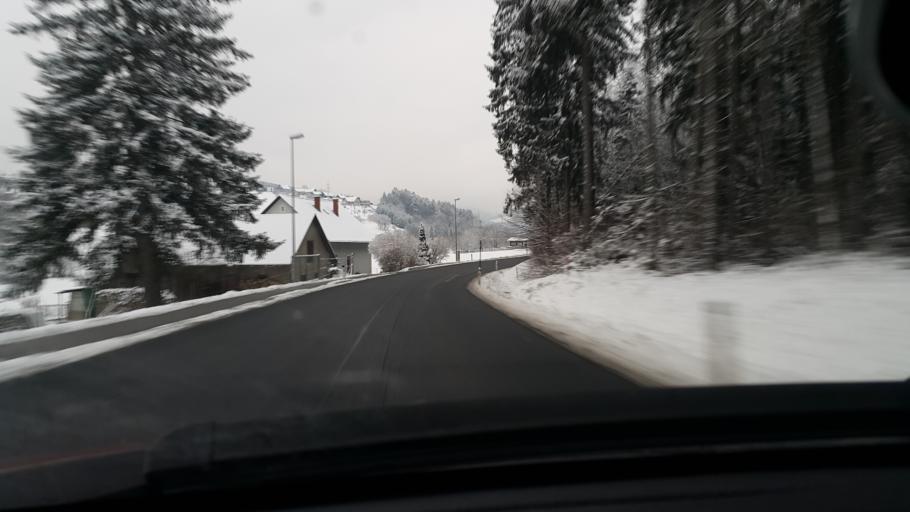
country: AT
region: Styria
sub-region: Politischer Bezirk Graz-Umgebung
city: Sankt Oswald bei Plankenwarth
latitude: 47.0579
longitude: 15.2827
